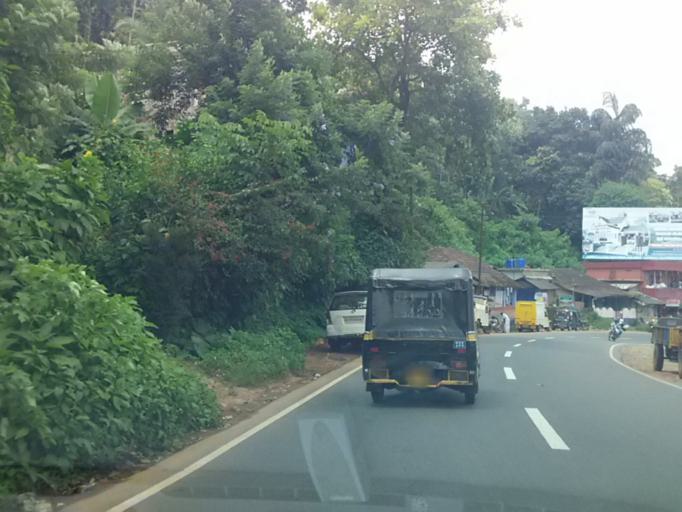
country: IN
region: Kerala
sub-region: Wayanad
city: Kalpetta
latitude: 11.5505
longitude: 76.0386
